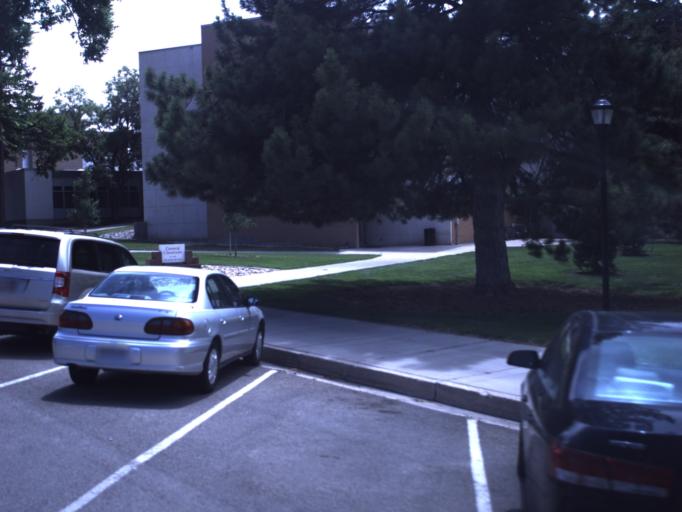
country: US
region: Utah
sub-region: Iron County
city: Cedar City
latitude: 37.6759
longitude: -113.0669
